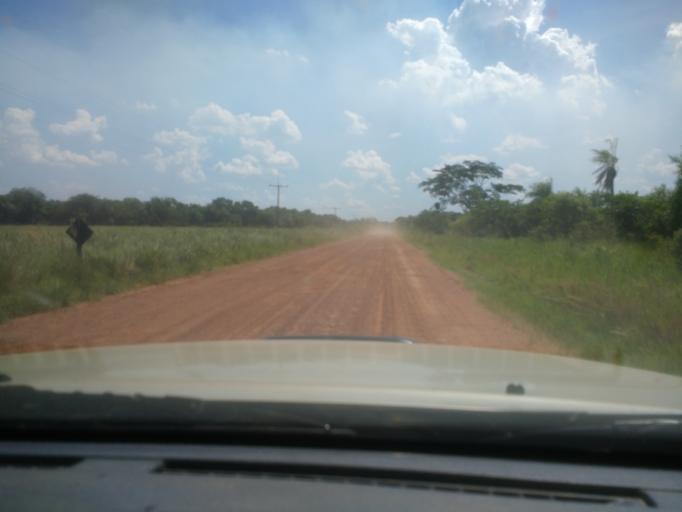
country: PY
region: San Pedro
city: Puerto Rosario
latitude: -24.3515
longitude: -57.1425
